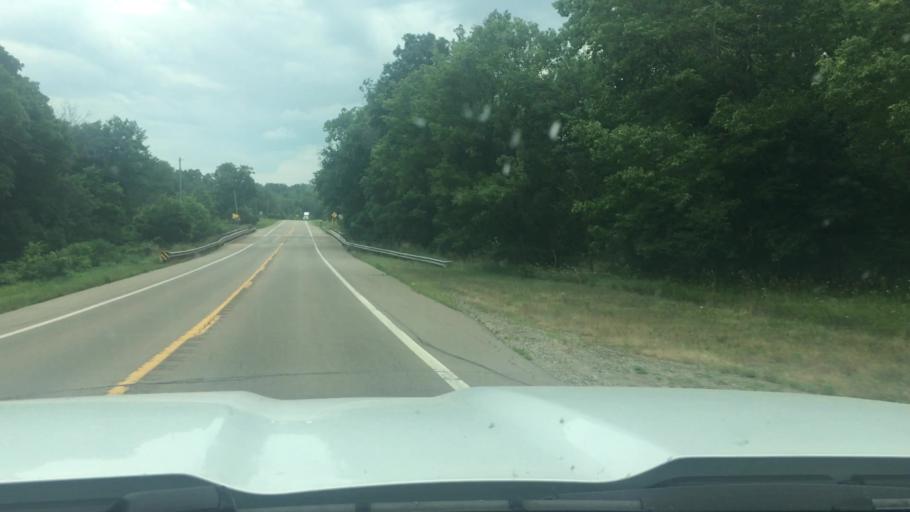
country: US
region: Michigan
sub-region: Ionia County
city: Portland
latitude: 42.9997
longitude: -84.9069
